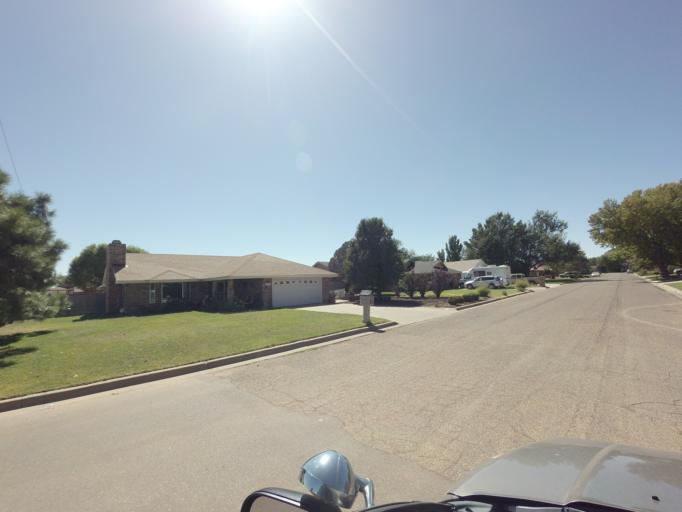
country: US
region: New Mexico
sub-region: Curry County
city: Clovis
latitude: 34.4414
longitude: -103.1787
